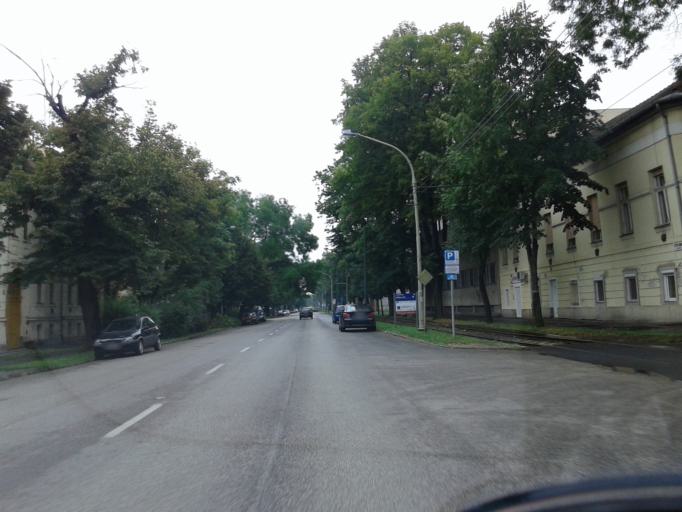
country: HU
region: Csongrad
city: Szeged
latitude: 46.2475
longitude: 20.1392
